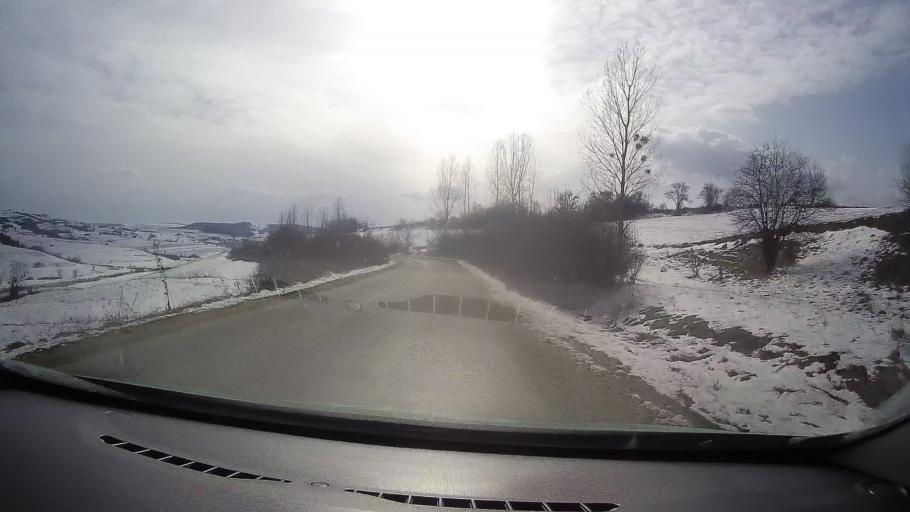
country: RO
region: Sibiu
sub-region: Comuna Bradeni
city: Bradeni
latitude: 46.1056
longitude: 24.8417
